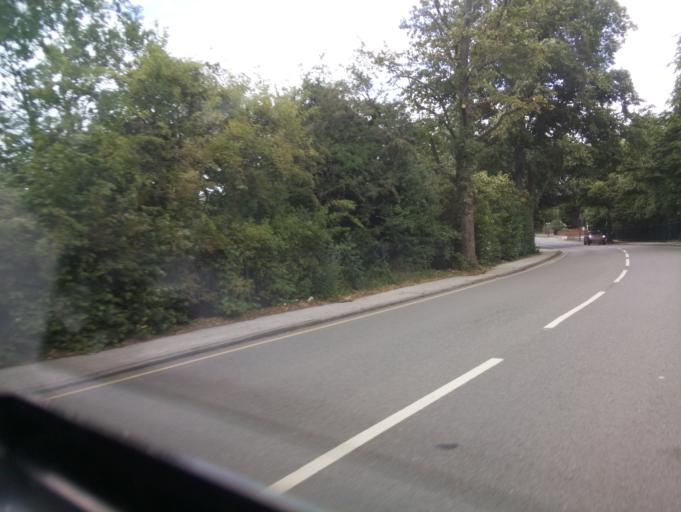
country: GB
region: England
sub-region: Warwickshire
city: Nuneaton
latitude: 52.5257
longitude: -1.4601
